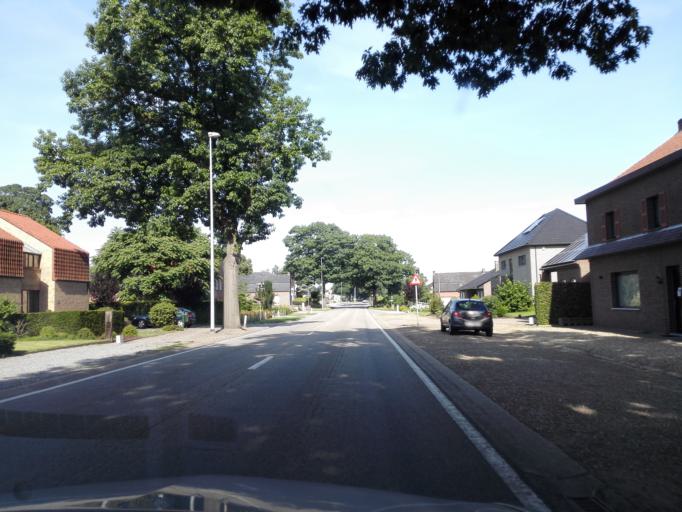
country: BE
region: Flanders
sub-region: Provincie Limburg
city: Bree
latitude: 51.0894
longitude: 5.6159
